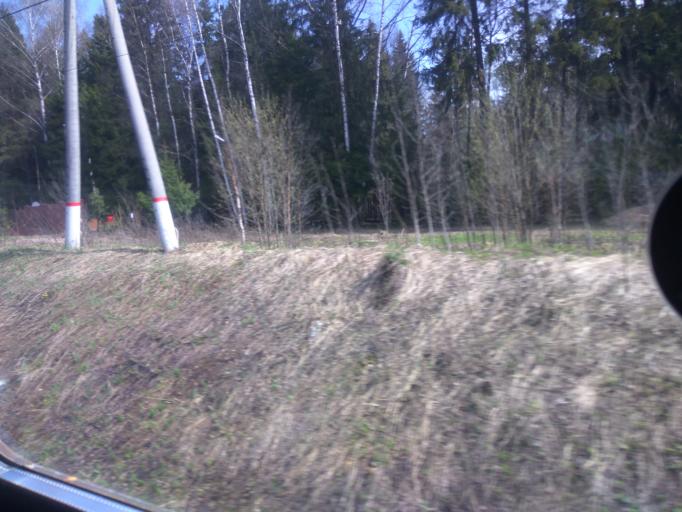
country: RU
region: Moskovskaya
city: Nekrasovskiy
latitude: 56.1123
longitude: 37.5123
